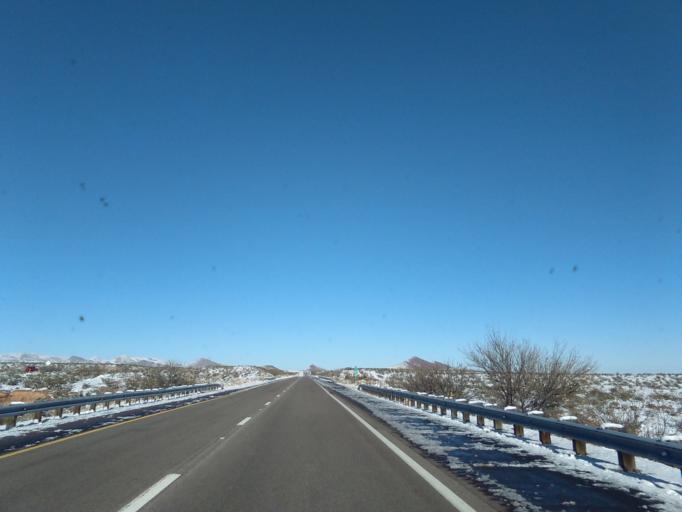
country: US
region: New Mexico
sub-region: Socorro County
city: Socorro
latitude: 33.7190
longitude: -107.0303
